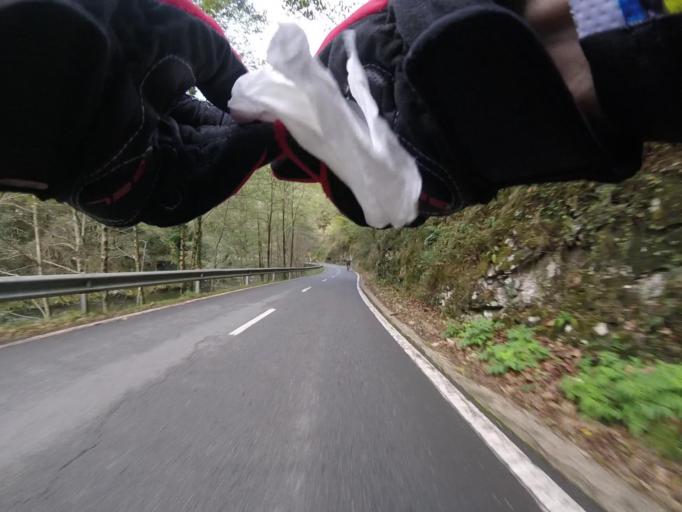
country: ES
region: Navarre
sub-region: Provincia de Navarra
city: Arano
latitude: 43.2099
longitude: -1.8694
